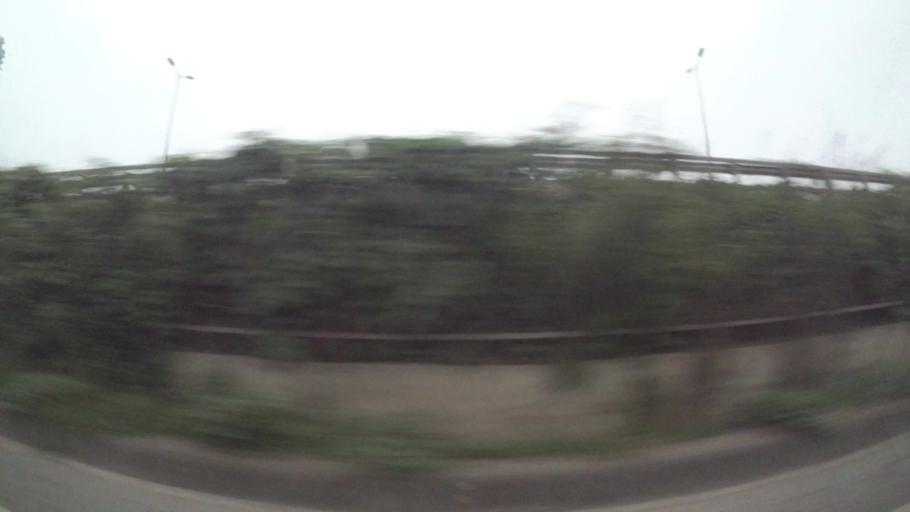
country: VN
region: Ha Noi
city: Van Dien
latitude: 20.9730
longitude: 105.8819
